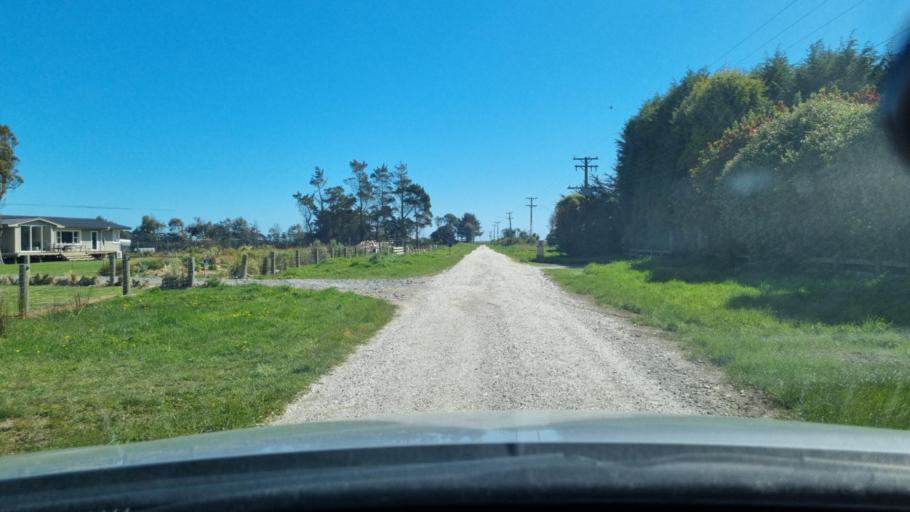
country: NZ
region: Southland
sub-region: Invercargill City
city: Invercargill
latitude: -46.3911
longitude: 168.2970
